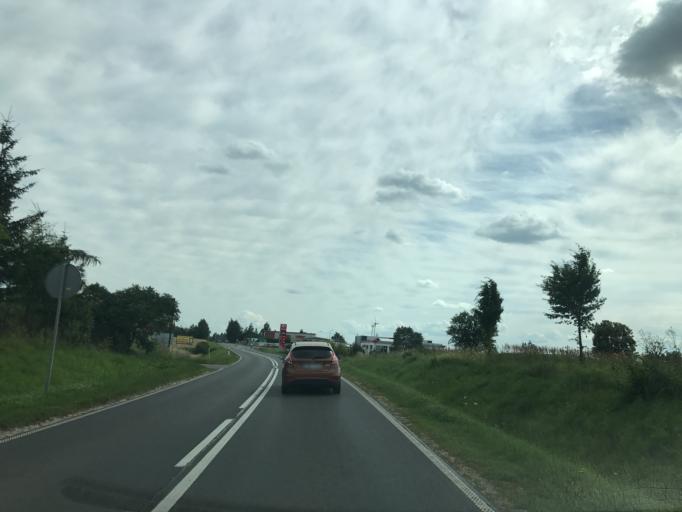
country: PL
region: Kujawsko-Pomorskie
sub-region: Powiat brodnicki
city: Brodnica
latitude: 53.2236
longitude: 19.3857
